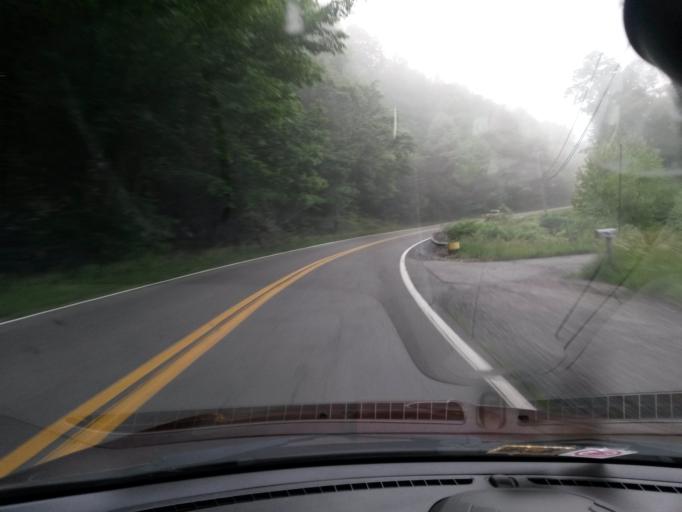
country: US
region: West Virginia
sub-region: McDowell County
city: Welch
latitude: 37.5021
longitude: -81.5504
